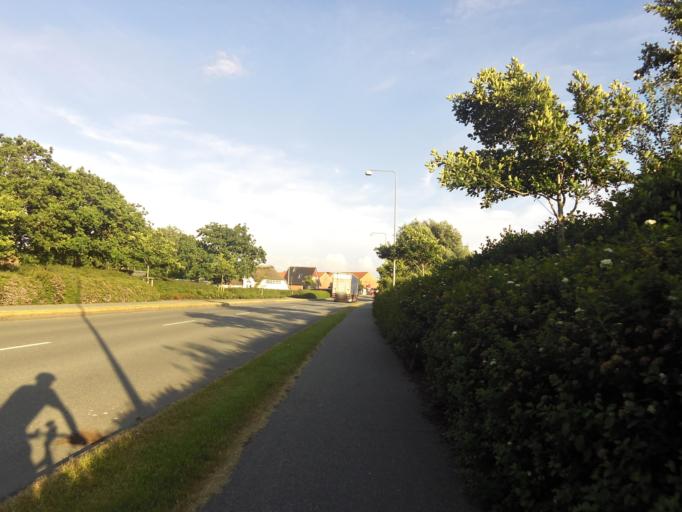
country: DK
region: South Denmark
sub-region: Tonder Kommune
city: Sherrebek
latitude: 55.1606
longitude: 8.7595
